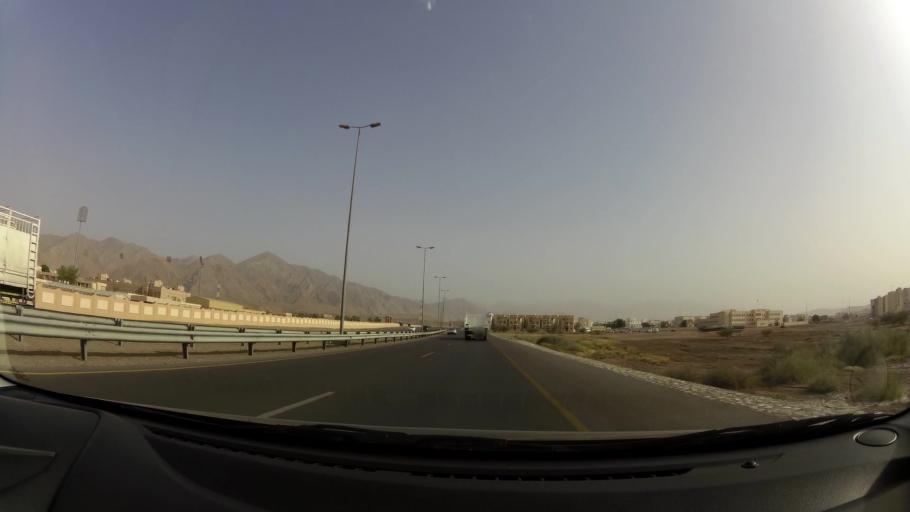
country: OM
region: Muhafazat Masqat
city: Bawshar
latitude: 23.5493
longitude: 58.3663
